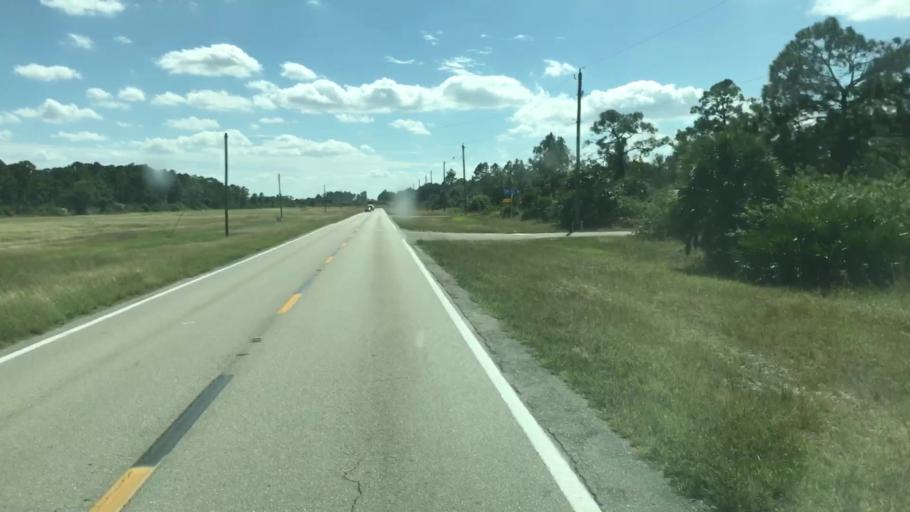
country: US
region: Florida
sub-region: Lee County
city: Lehigh Acres
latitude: 26.6506
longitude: -81.6634
